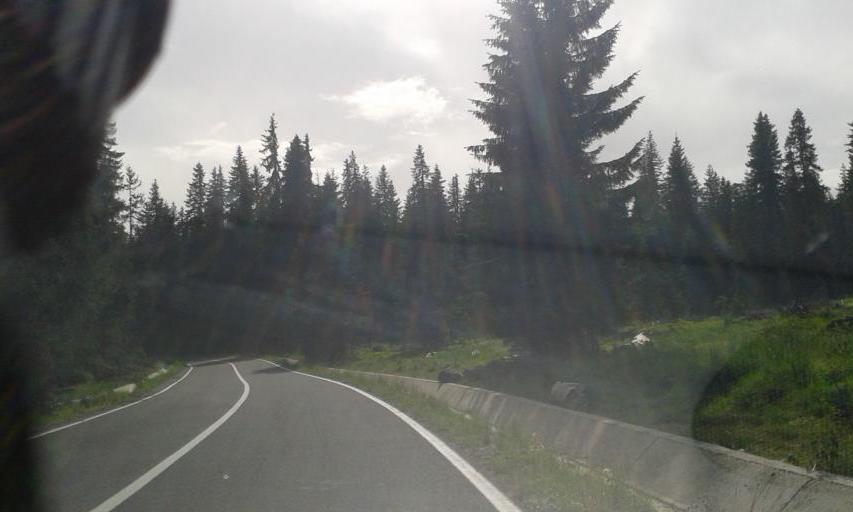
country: RO
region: Hunedoara
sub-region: Oras Petrila
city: Petrila
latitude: 45.4838
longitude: 23.6386
